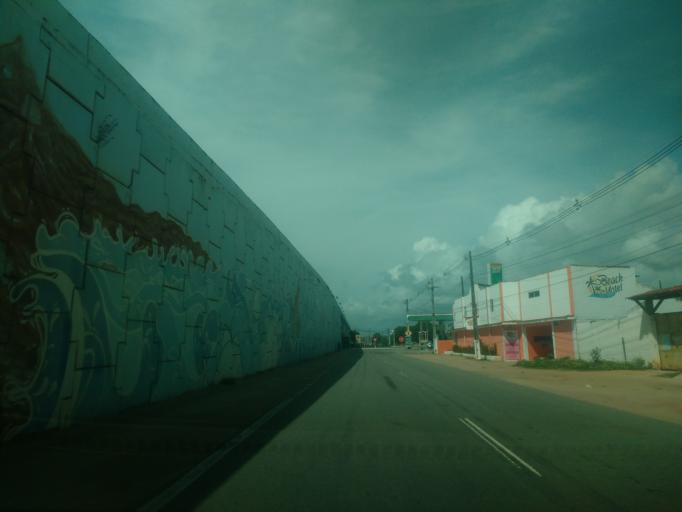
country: BR
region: Alagoas
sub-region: Marechal Deodoro
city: Marechal Deodoro
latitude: -9.7658
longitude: -35.8502
